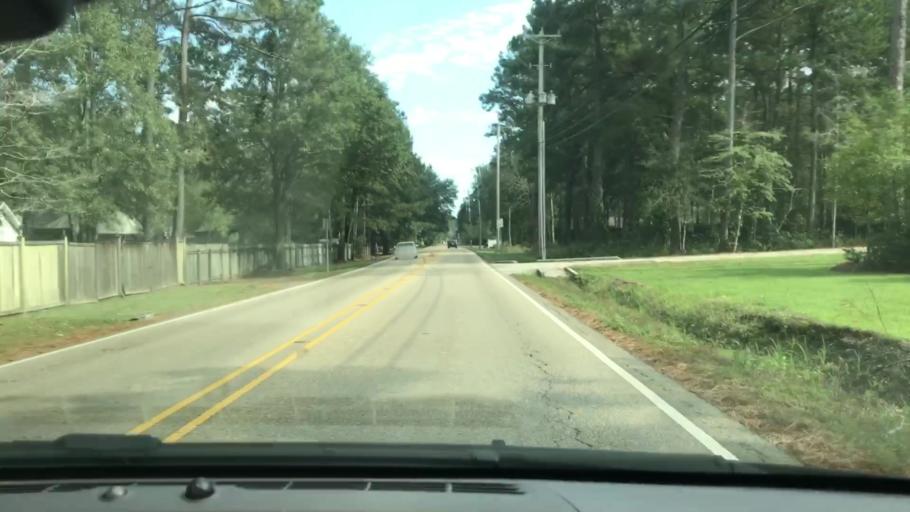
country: US
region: Louisiana
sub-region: Saint Tammany Parish
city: Abita Springs
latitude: 30.4599
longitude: -90.0520
